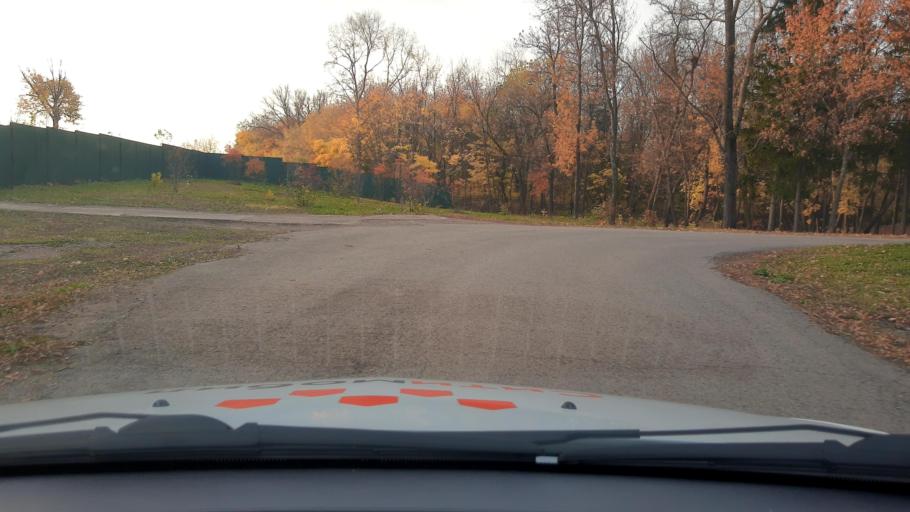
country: RU
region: Bashkortostan
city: Ufa
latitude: 54.7120
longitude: 56.0169
